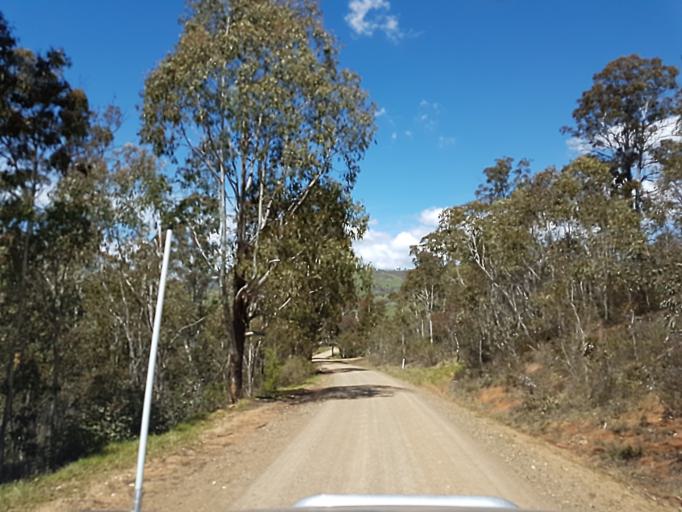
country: AU
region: Victoria
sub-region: Alpine
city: Mount Beauty
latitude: -37.0874
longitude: 147.4047
